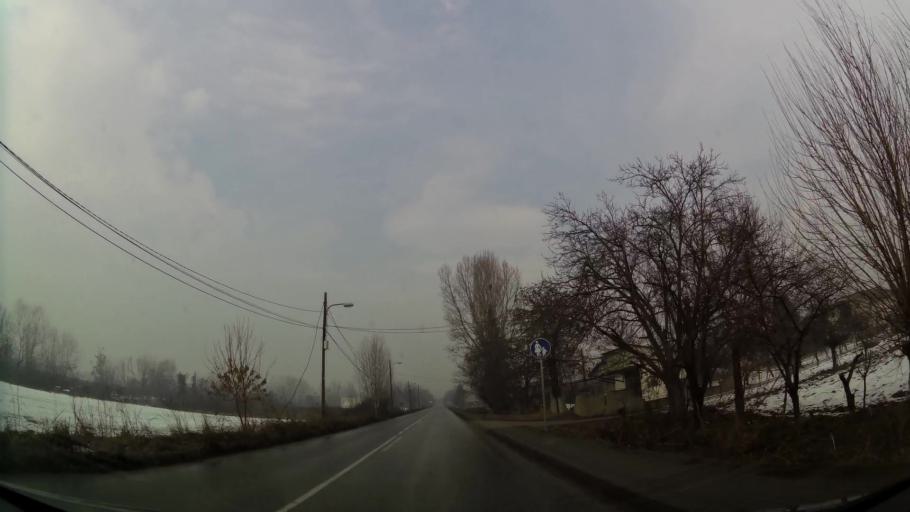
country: MK
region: Ilinden
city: Jurumleri
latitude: 41.9731
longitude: 21.5401
